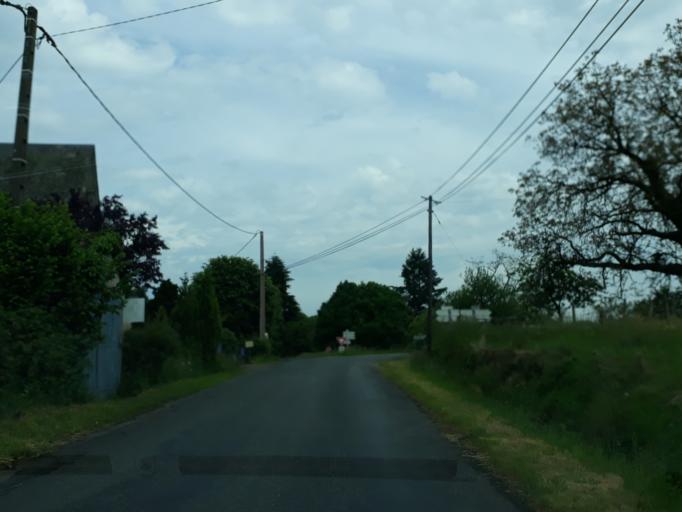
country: FR
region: Limousin
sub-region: Departement de la Correze
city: Beynat
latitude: 45.1051
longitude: 1.7760
